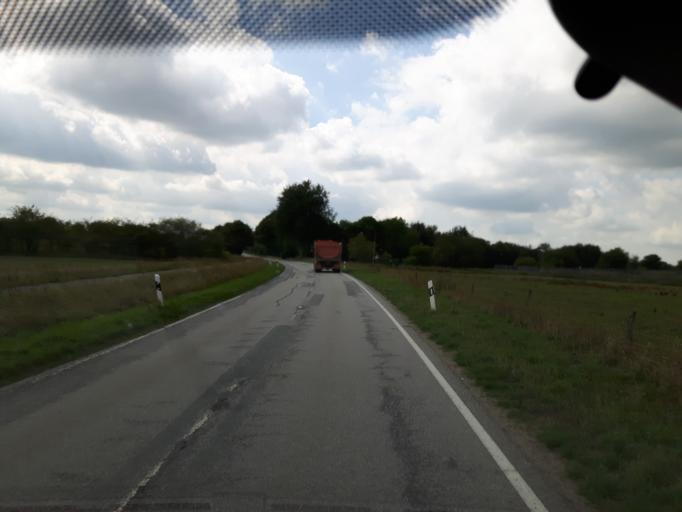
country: DE
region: Schleswig-Holstein
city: Handewitt
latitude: 54.7992
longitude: 9.3407
